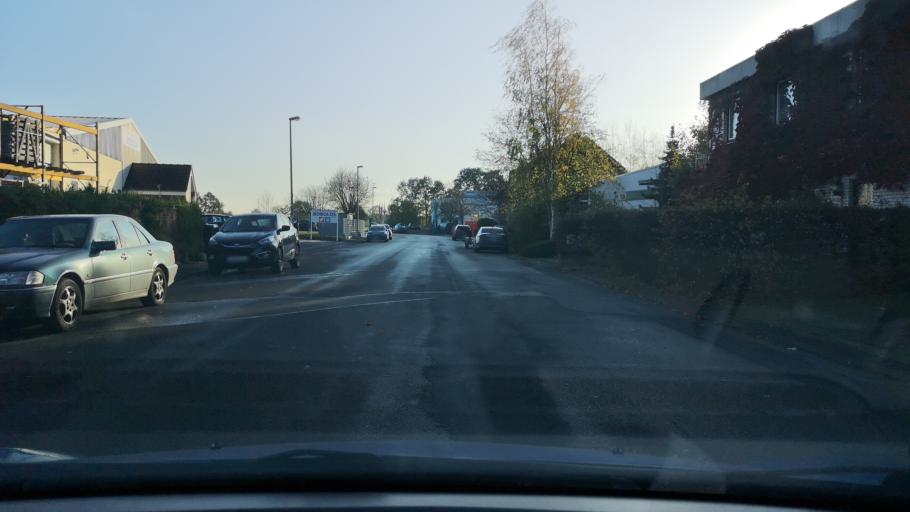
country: DE
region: Lower Saxony
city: Langenhagen
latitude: 52.4514
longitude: 9.7861
